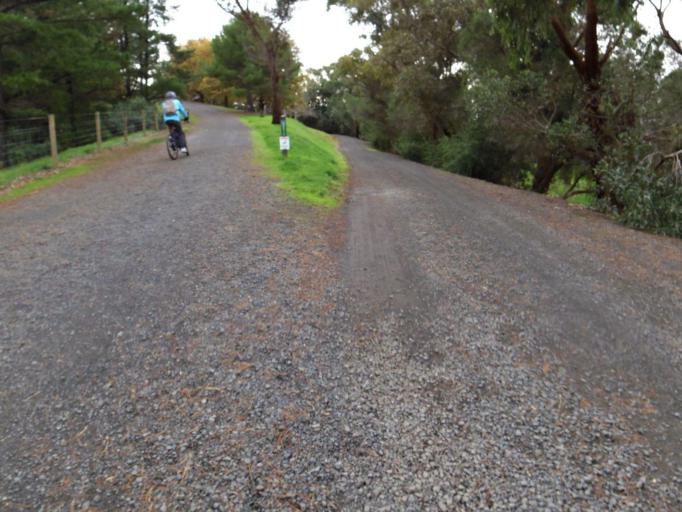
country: AU
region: Victoria
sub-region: Casey
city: Berwick
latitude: -38.0249
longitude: 145.3428
